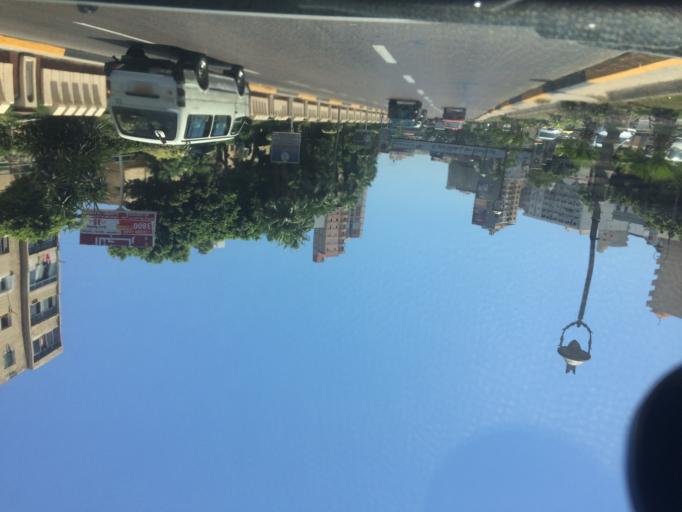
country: EG
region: Alexandria
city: Alexandria
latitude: 31.1952
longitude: 29.9212
